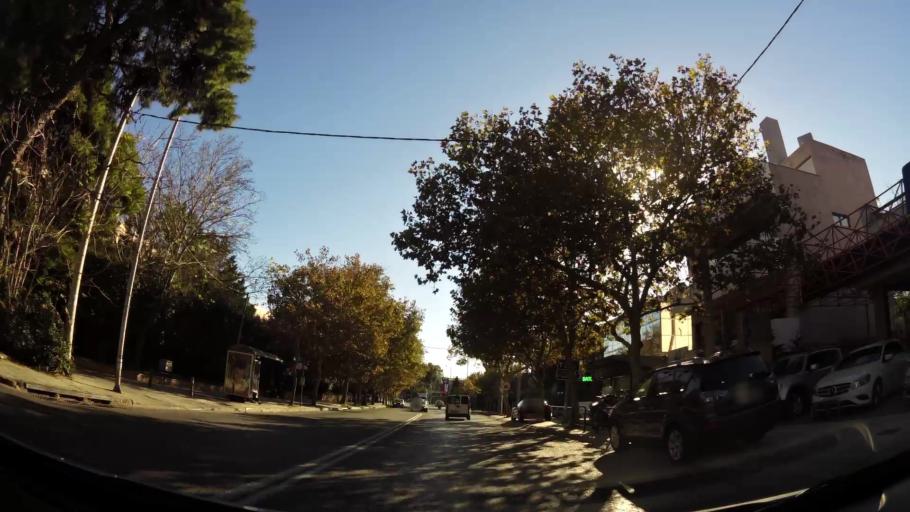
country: GR
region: Attica
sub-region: Nomarchia Athinas
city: Kifisia
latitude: 38.0771
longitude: 23.8125
